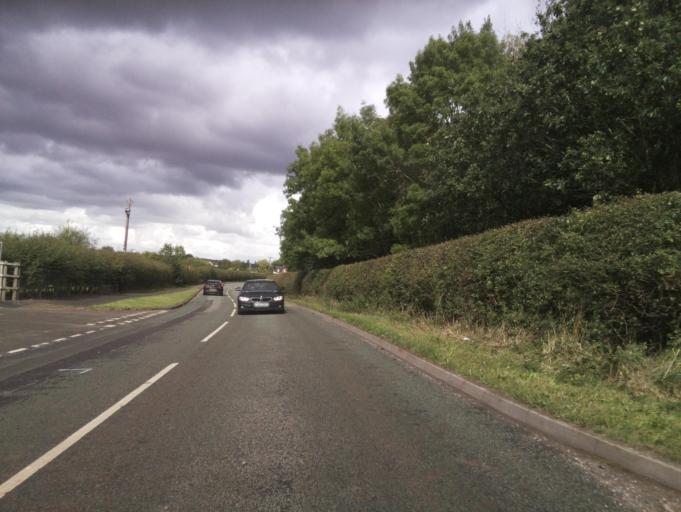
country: GB
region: England
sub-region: Staffordshire
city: Eccleshall
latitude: 52.8813
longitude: -2.2361
